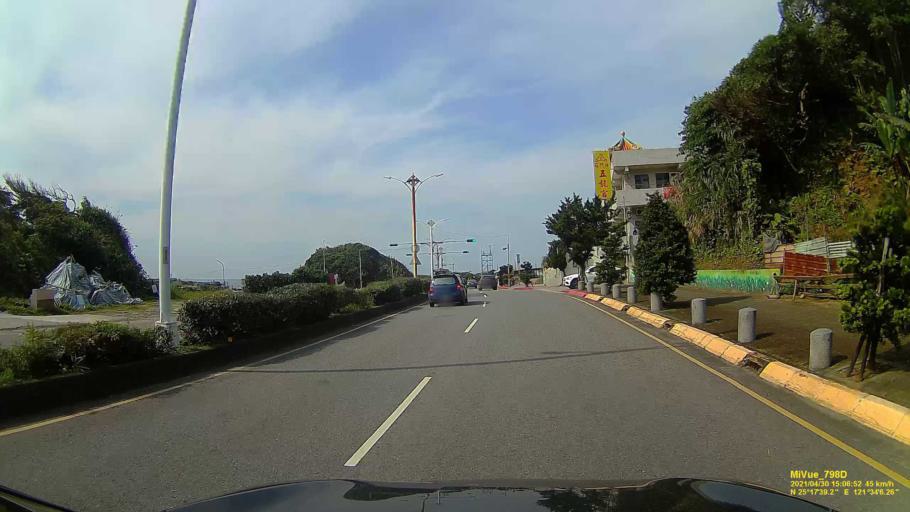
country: TW
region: Taiwan
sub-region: Keelung
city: Keelung
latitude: 25.2945
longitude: 121.5685
